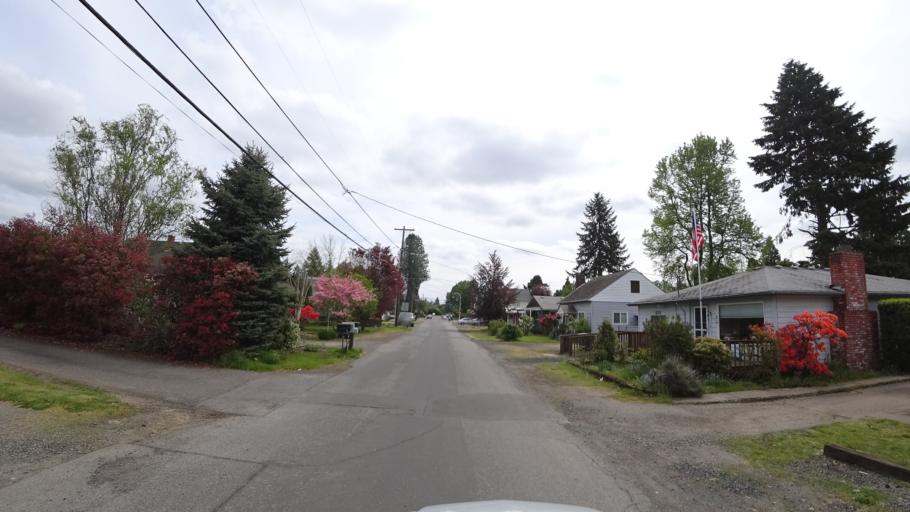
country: US
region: Oregon
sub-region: Washington County
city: Hillsboro
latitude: 45.5286
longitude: -122.9951
